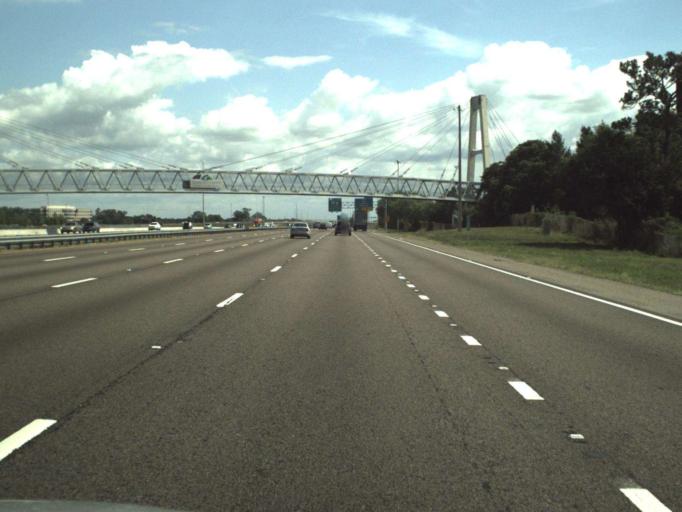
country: US
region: Florida
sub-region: Seminole County
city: Heathrow
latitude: 28.7776
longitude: -81.3546
